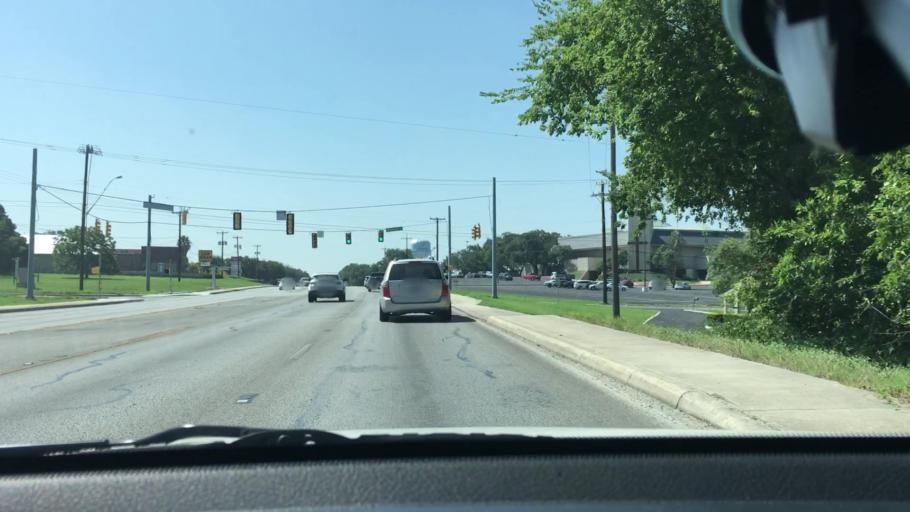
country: US
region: Texas
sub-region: Bexar County
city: Castle Hills
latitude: 29.5370
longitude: -98.5258
